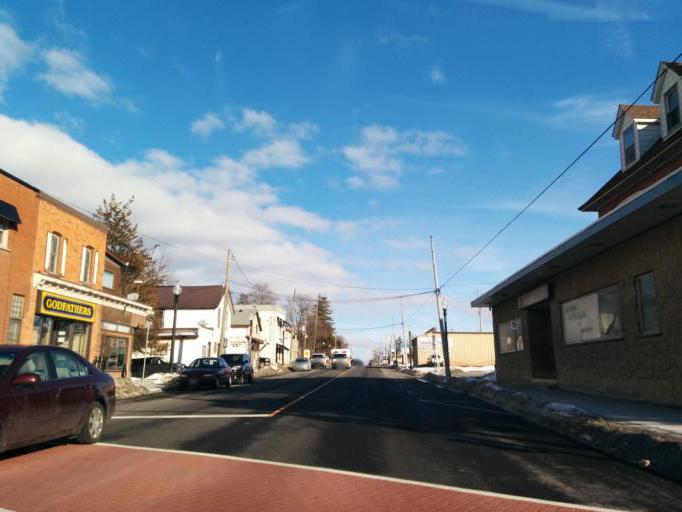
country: CA
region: Ontario
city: Ancaster
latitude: 42.9496
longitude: -79.8586
